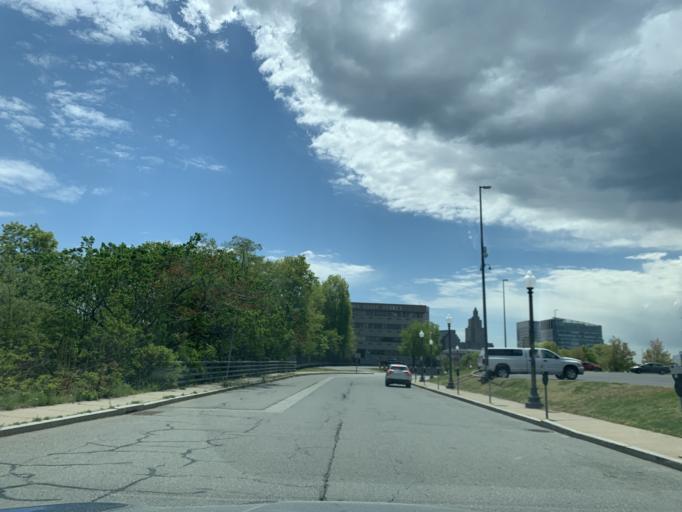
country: US
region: Rhode Island
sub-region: Providence County
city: Providence
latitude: 41.8337
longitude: -71.4138
